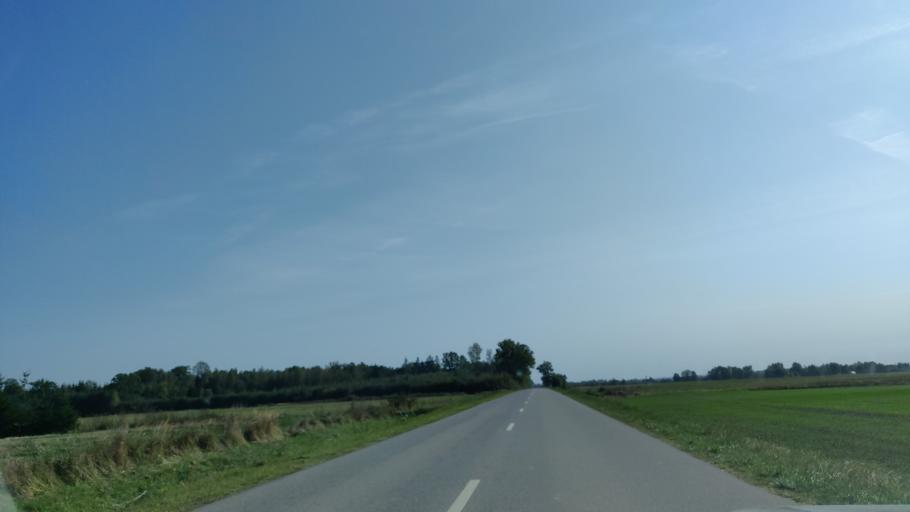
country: LT
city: Sirvintos
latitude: 54.9712
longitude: 24.8179
